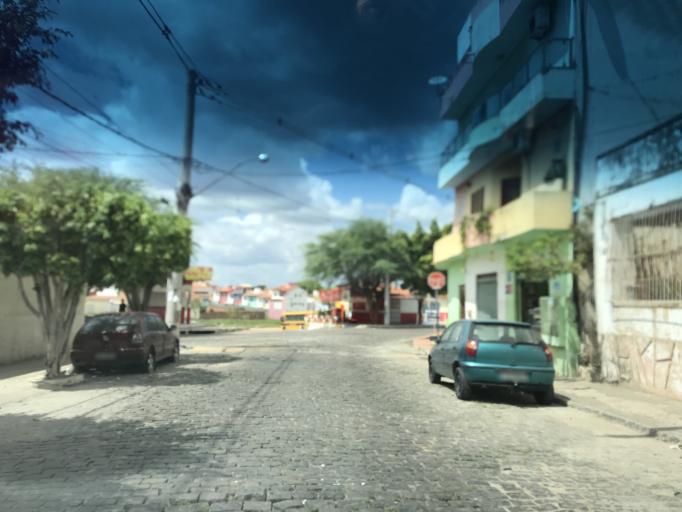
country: BR
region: Bahia
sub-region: Itaberaba
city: Itaberaba
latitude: -12.5329
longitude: -40.3049
